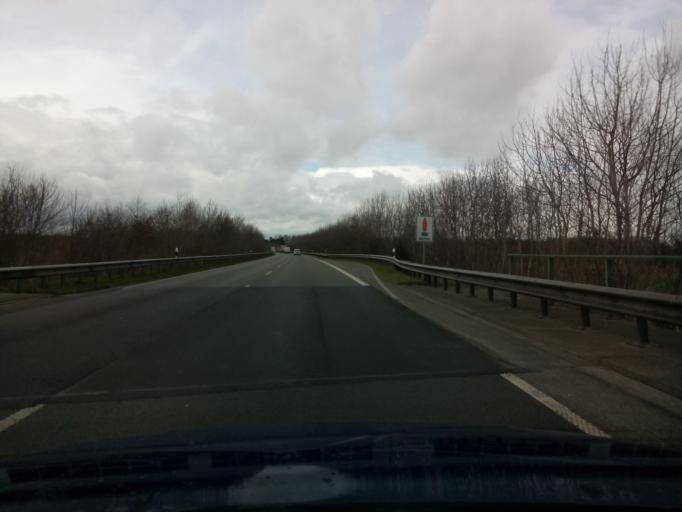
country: DE
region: Lower Saxony
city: Meppen
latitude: 52.7260
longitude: 7.2538
